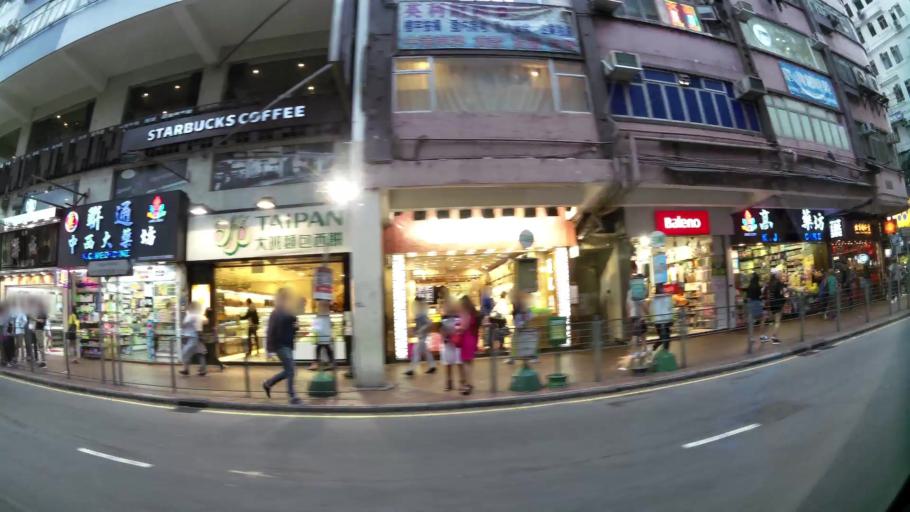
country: HK
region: Kowloon City
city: Kowloon
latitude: 22.3196
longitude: 114.1716
